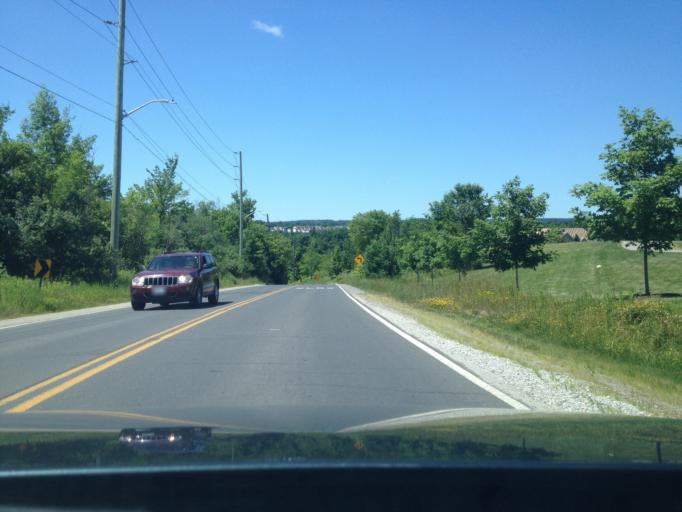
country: CA
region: Ontario
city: Brampton
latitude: 43.6639
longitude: -79.9066
